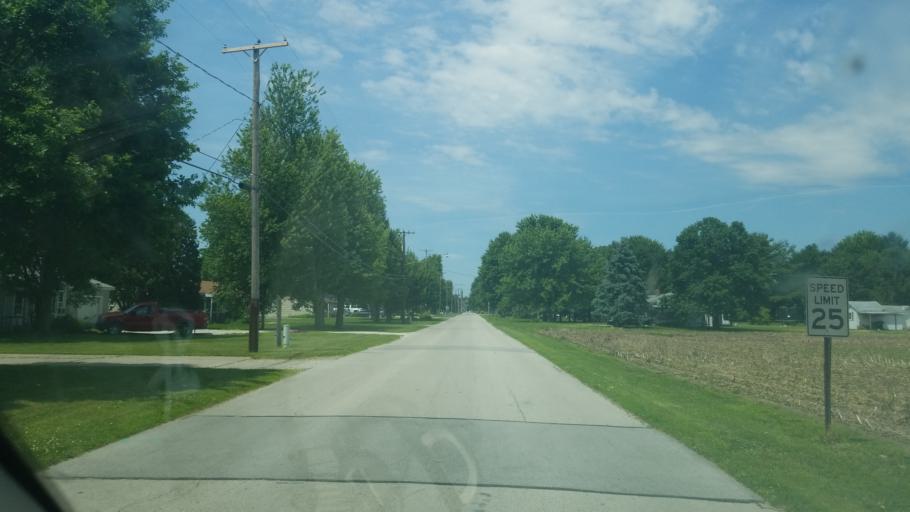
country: US
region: Ohio
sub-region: Wood County
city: North Baltimore
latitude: 41.2537
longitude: -83.5963
